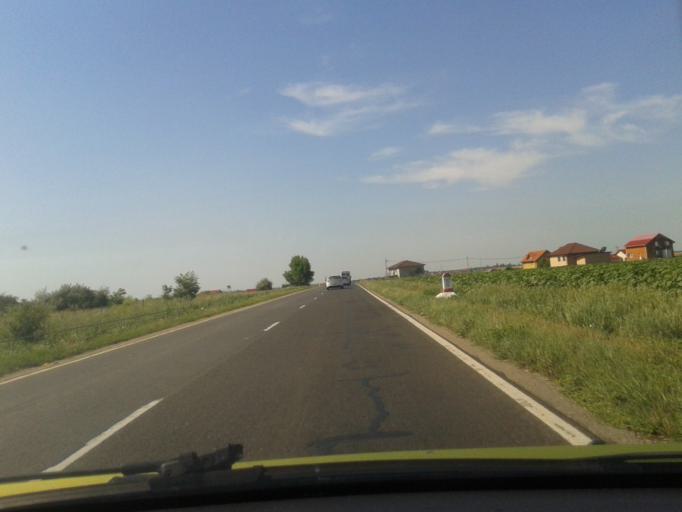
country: RO
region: Constanta
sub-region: Municipiul Mangalia
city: Mangalia
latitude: 43.7653
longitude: 28.5740
